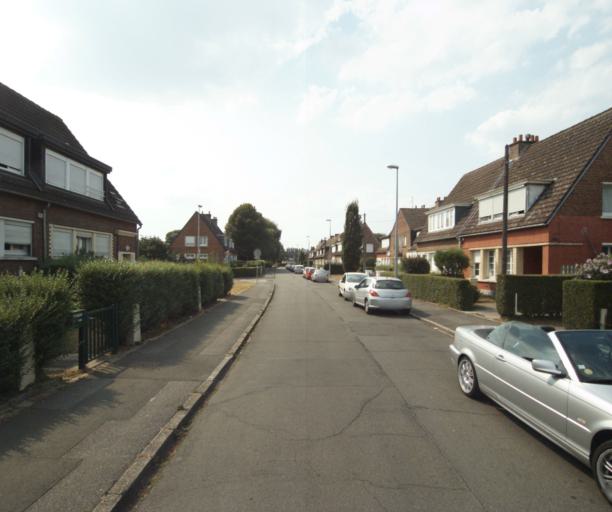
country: FR
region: Nord-Pas-de-Calais
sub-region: Departement du Nord
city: Neuville-en-Ferrain
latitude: 50.7341
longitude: 3.1387
